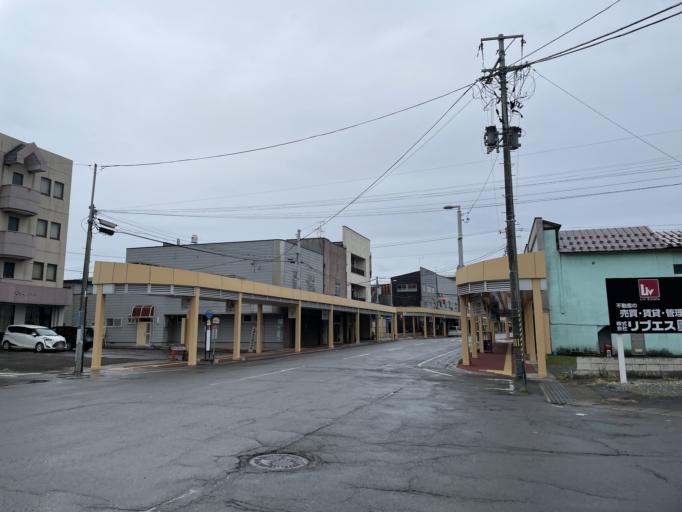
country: JP
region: Akita
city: Takanosu
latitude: 40.2319
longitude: 140.3697
